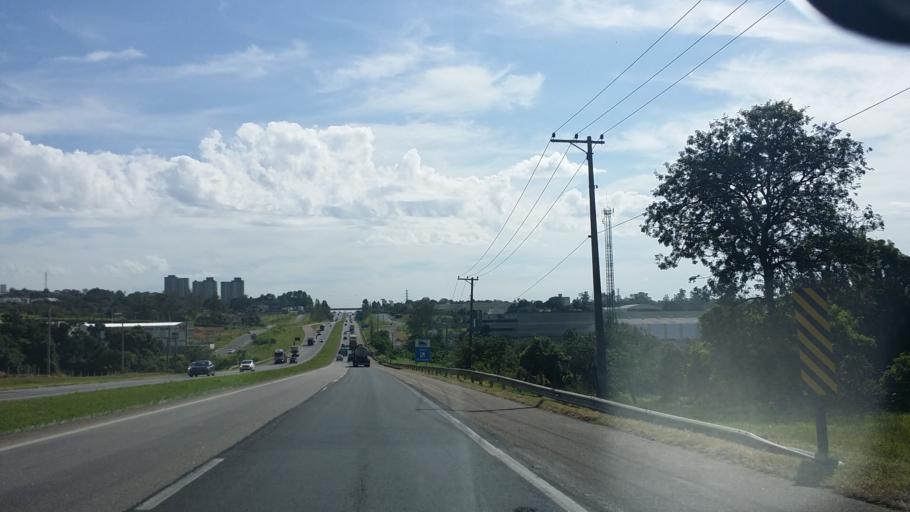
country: BR
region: Sao Paulo
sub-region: Indaiatuba
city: Indaiatuba
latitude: -23.1047
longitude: -47.2012
